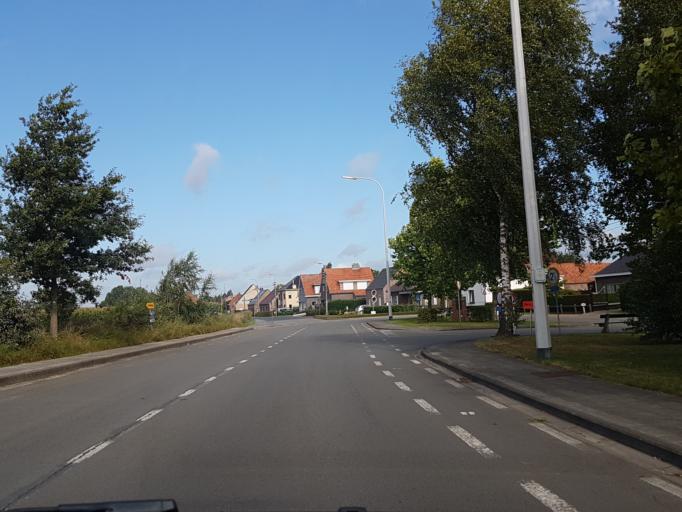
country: BE
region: Flanders
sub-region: Provincie Oost-Vlaanderen
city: Nevele
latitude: 51.0576
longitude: 3.5659
